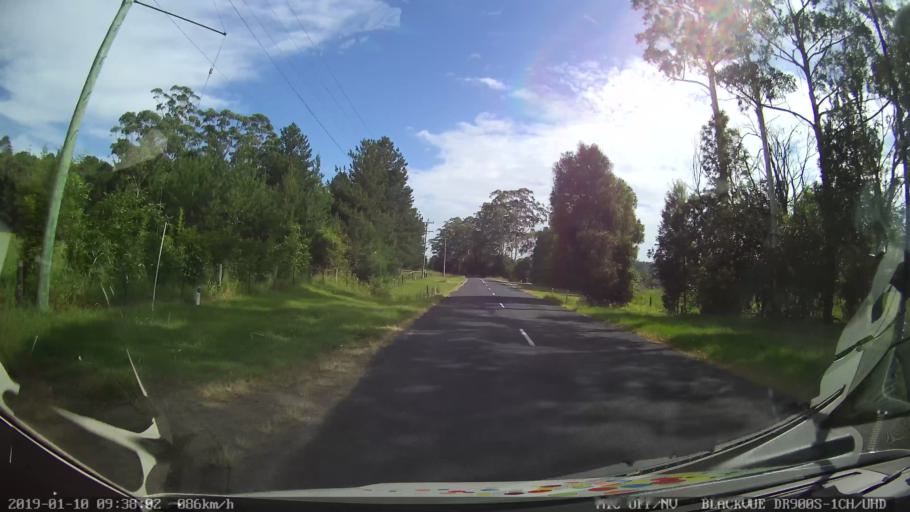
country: AU
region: New South Wales
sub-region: Coffs Harbour
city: Nana Glen
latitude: -30.1807
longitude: 153.0071
